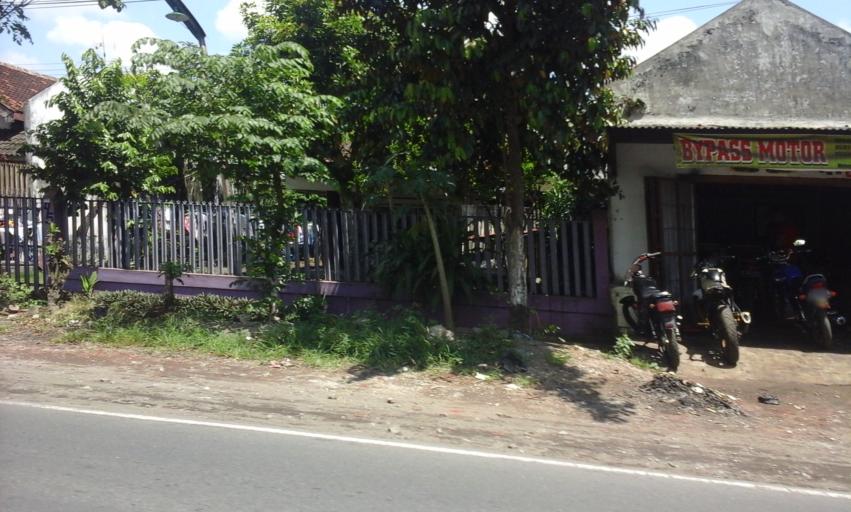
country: ID
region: East Java
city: Sumberketangi
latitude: -8.1877
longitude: 113.7495
